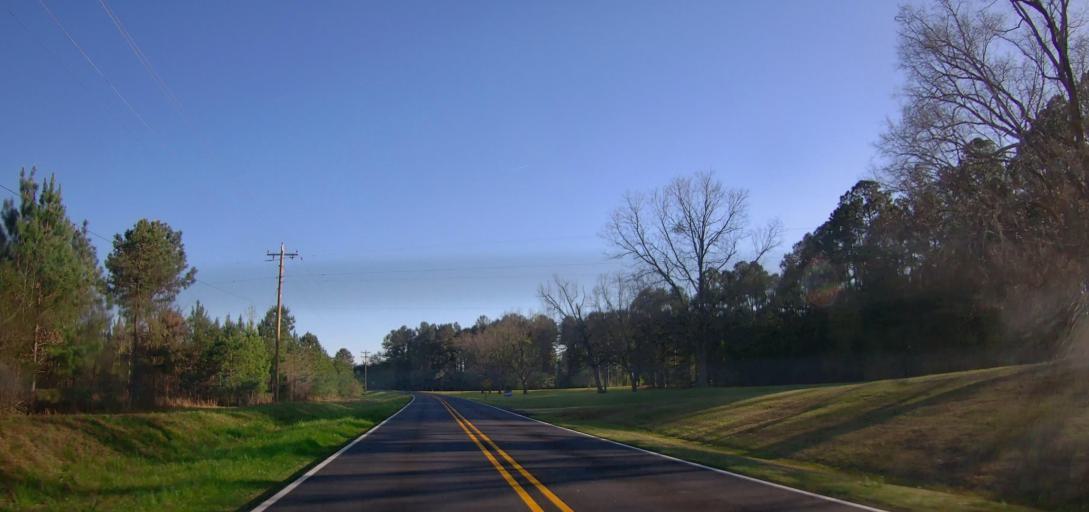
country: US
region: Georgia
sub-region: Butts County
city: Jackson
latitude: 33.3374
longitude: -83.9101
